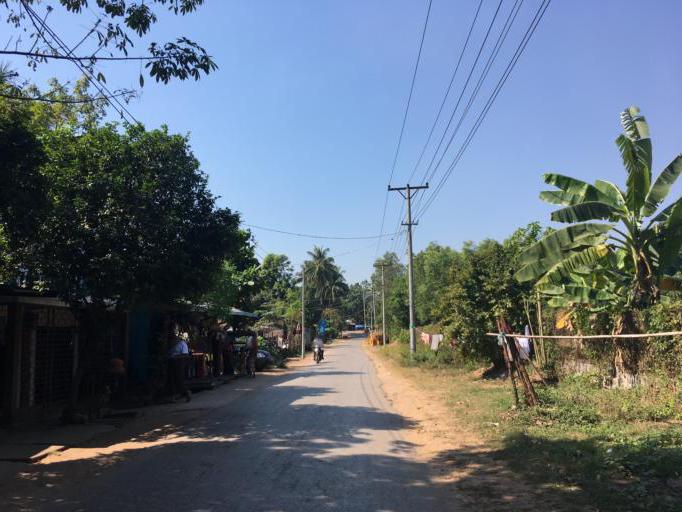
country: MM
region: Mon
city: Mawlamyine
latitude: 16.4340
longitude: 97.6985
